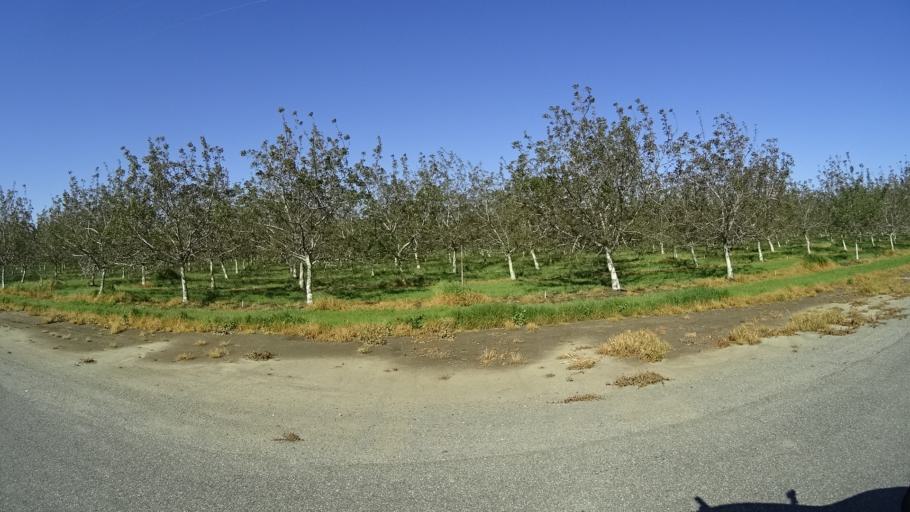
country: US
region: California
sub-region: Glenn County
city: Hamilton City
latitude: 39.6851
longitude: -122.0743
